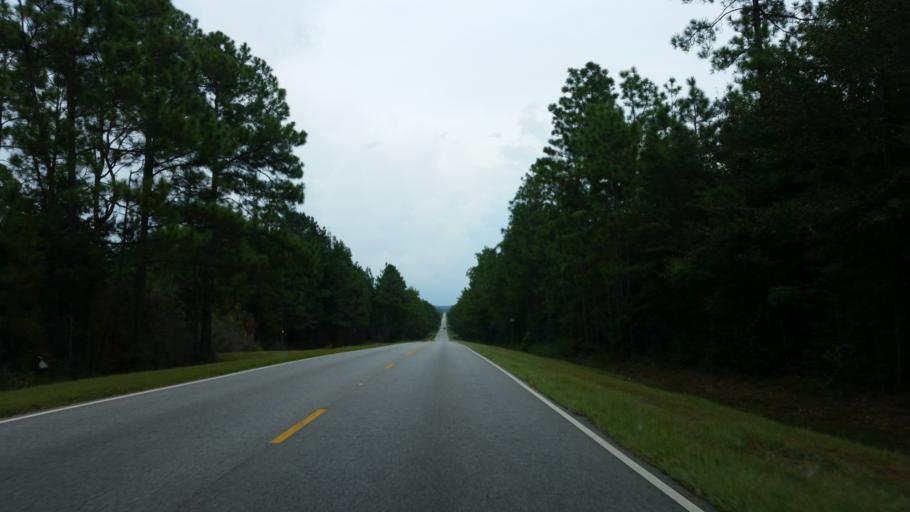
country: US
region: Florida
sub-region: Escambia County
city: Molino
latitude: 30.6623
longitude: -87.2977
